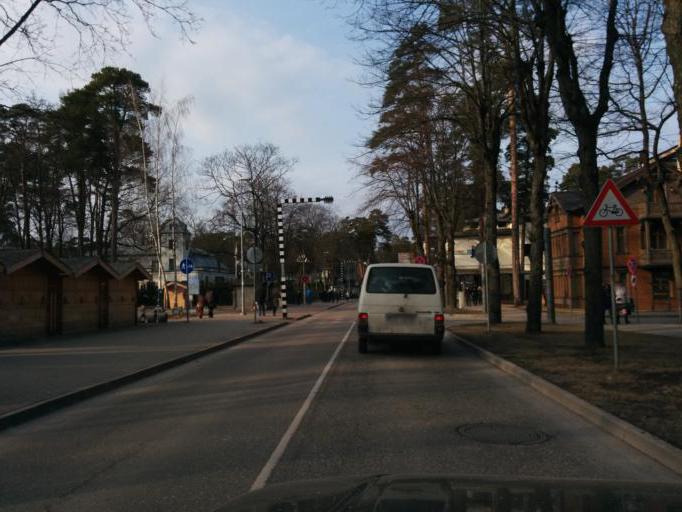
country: LV
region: Jurmala
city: Jurmala
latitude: 56.9757
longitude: 23.8128
